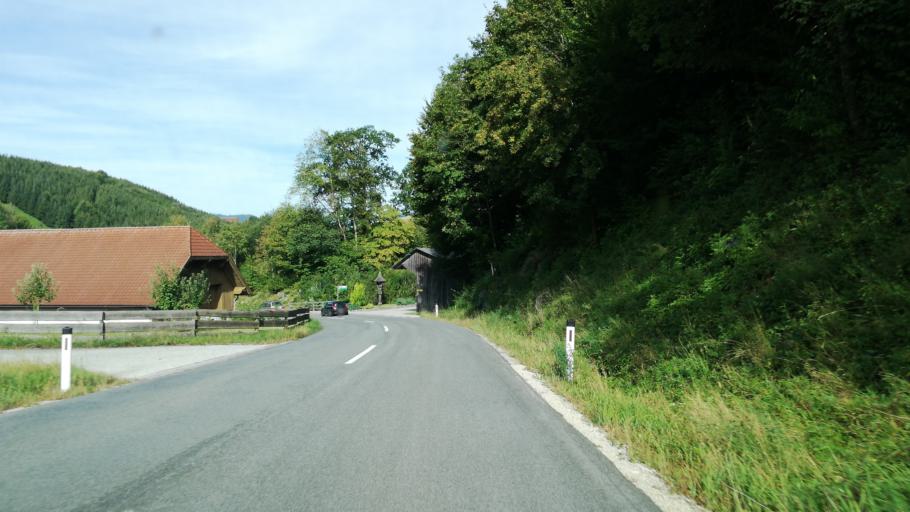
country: AT
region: Lower Austria
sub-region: Politischer Bezirk Amstetten
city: Behamberg
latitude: 47.9861
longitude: 14.5413
